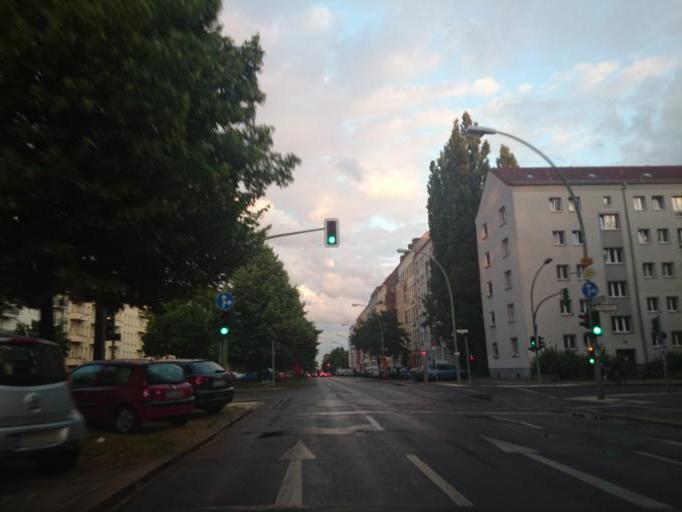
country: DE
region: Berlin
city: Friedrichshain Bezirk
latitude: 52.5246
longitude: 13.4487
